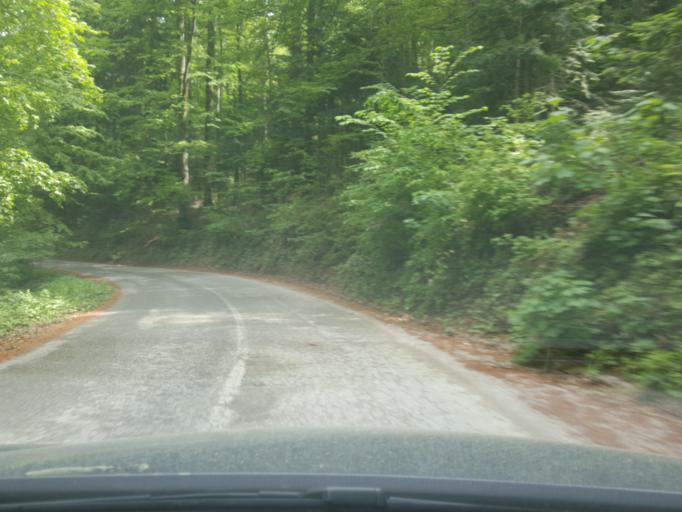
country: RS
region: Central Serbia
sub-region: Zlatiborski Okrug
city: Bajina Basta
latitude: 43.9183
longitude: 19.4873
